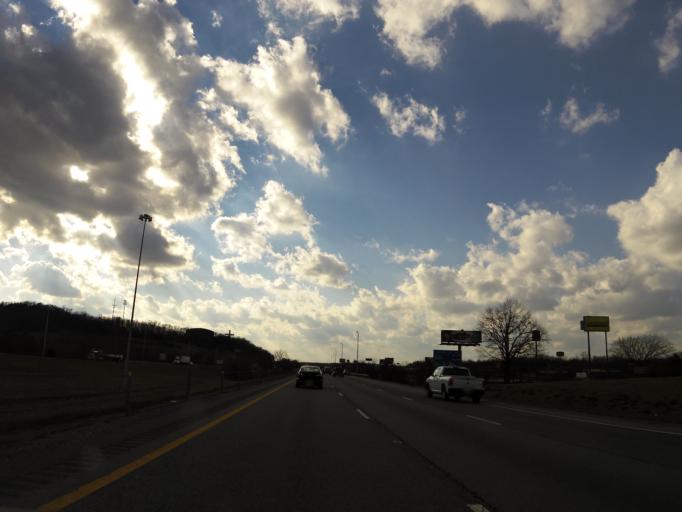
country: US
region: Tennessee
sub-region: Putnam County
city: Cookeville
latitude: 36.1359
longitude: -85.5059
